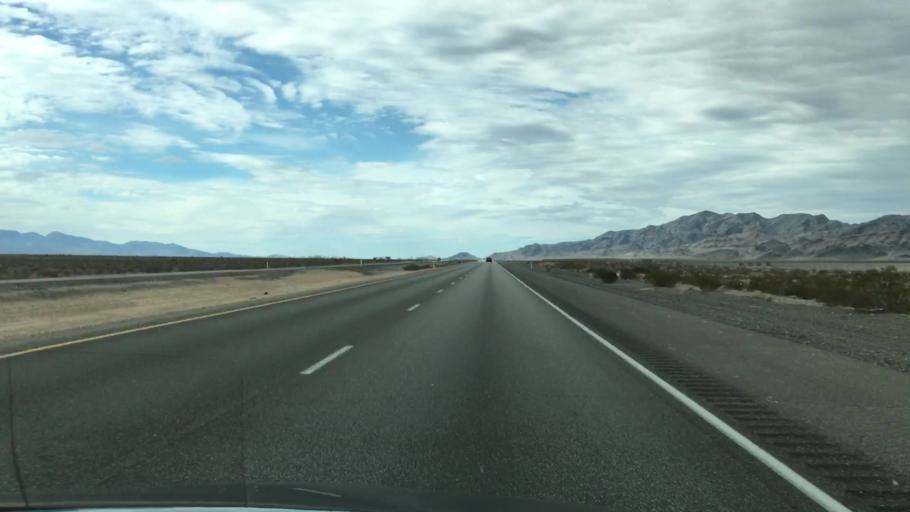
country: US
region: Nevada
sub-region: Nye County
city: Pahrump
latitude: 36.5797
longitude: -115.6940
